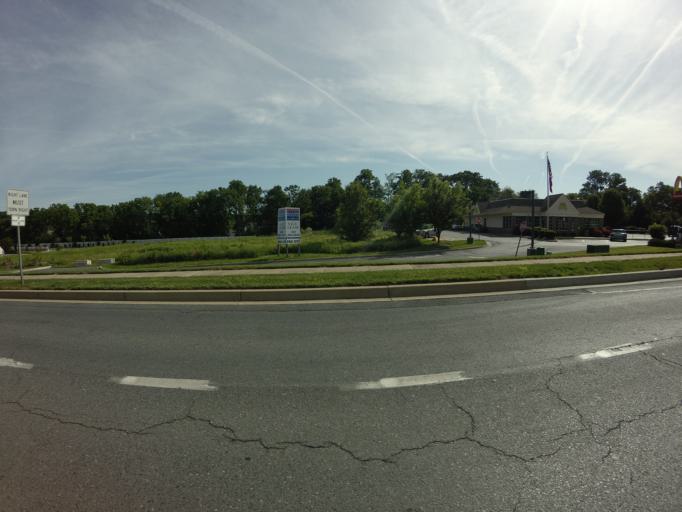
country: US
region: Maryland
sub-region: Frederick County
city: Linganore
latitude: 39.3849
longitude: -77.2576
